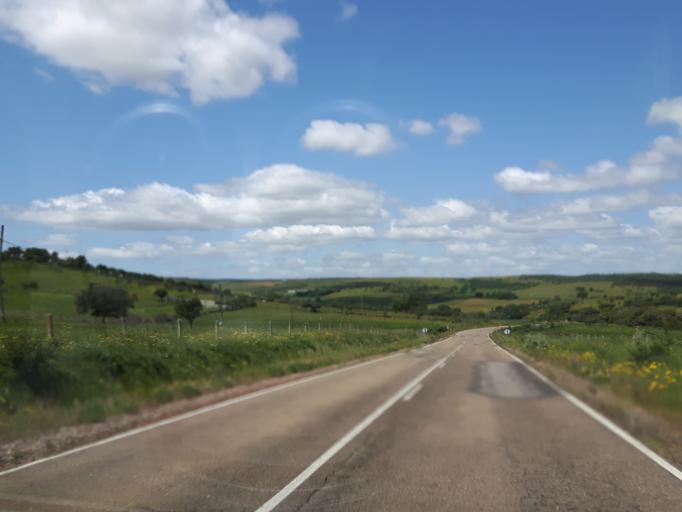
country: ES
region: Castille and Leon
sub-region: Provincia de Salamanca
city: Aldea del Obispo
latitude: 40.7224
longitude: -6.7678
